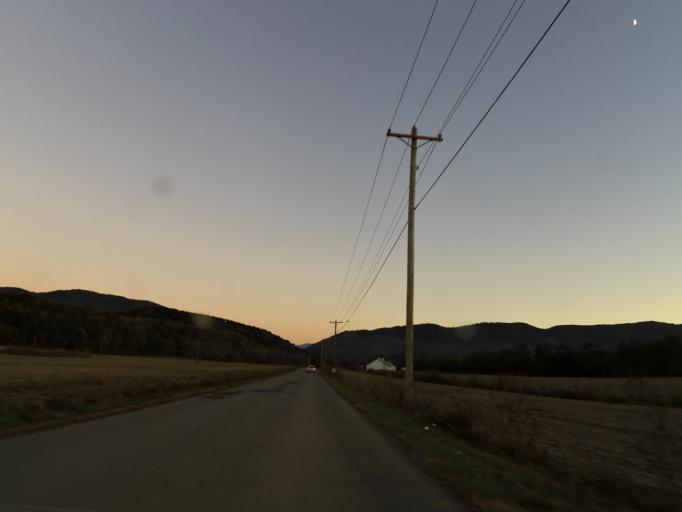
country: US
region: Tennessee
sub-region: Blount County
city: Wildwood
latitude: 35.7597
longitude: -83.8450
